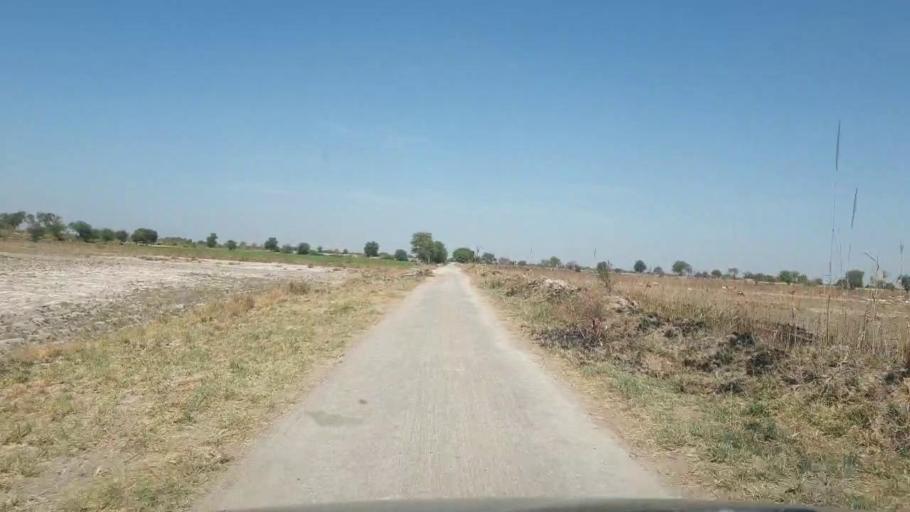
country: PK
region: Sindh
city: Dhoro Naro
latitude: 25.4538
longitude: 69.6085
